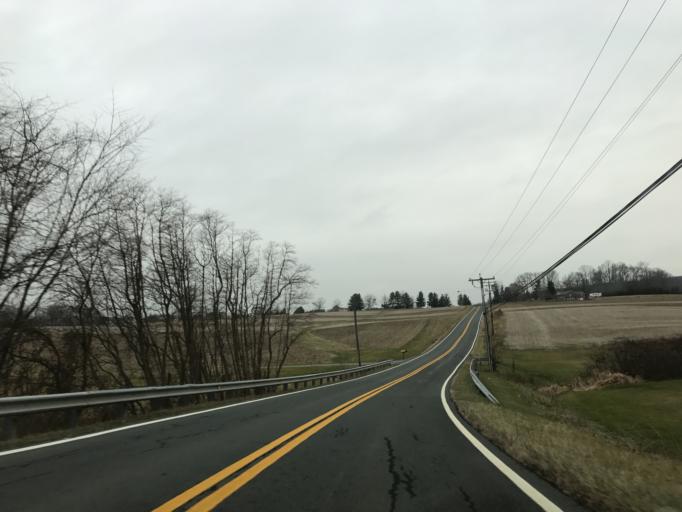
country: US
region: Maryland
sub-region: Carroll County
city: Westminster
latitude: 39.5265
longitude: -77.0338
